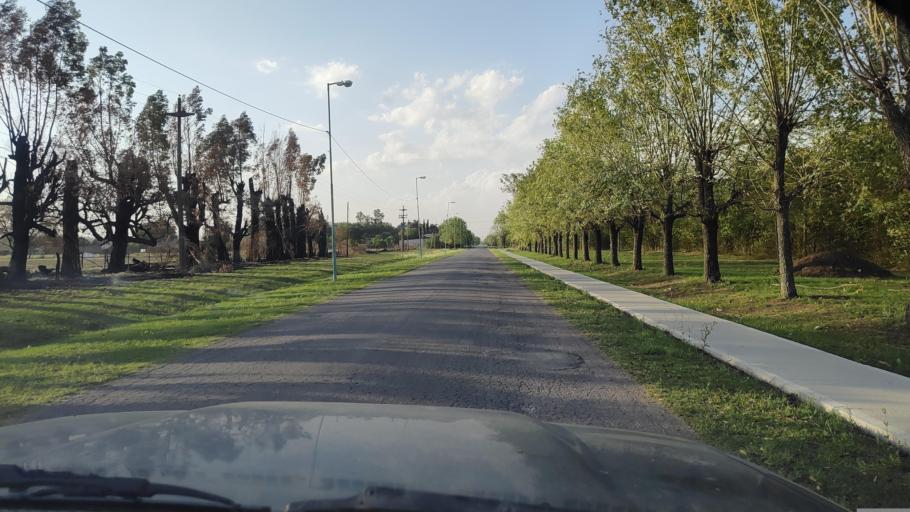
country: AR
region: Buenos Aires
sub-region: Partido de Lujan
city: Lujan
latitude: -34.5530
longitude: -59.2067
